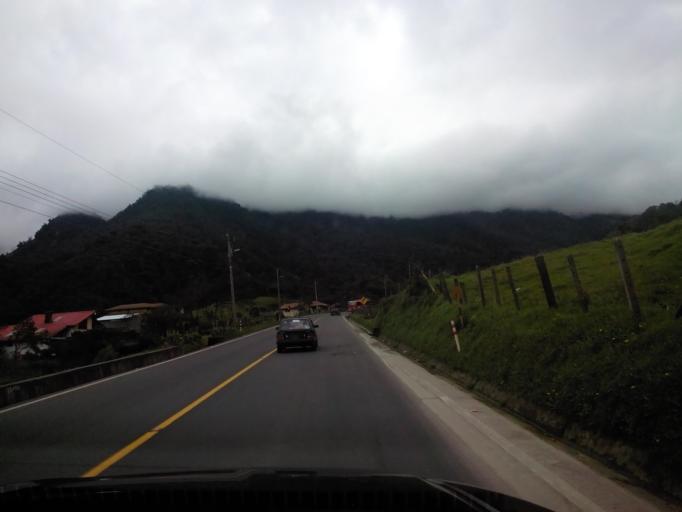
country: EC
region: Pichincha
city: Sangolqui
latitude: -0.3779
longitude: -78.1253
